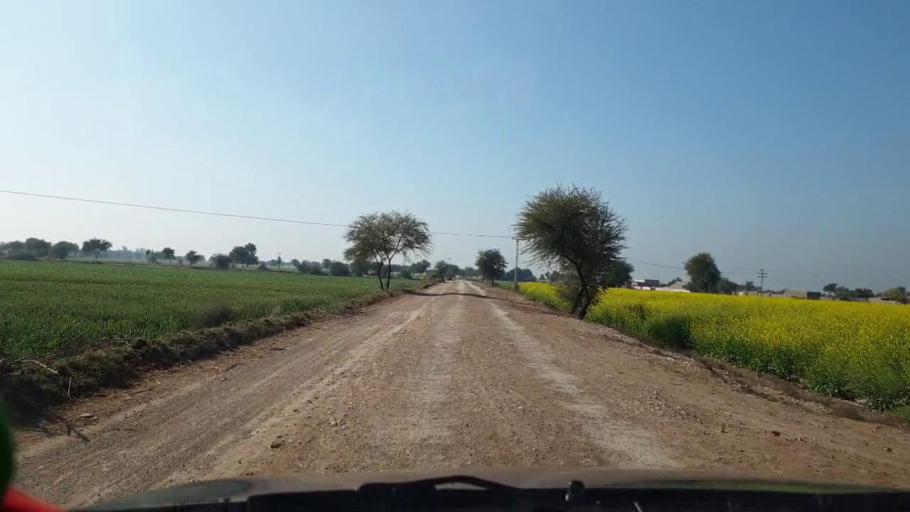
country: PK
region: Sindh
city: Sinjhoro
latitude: 25.9848
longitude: 68.7455
